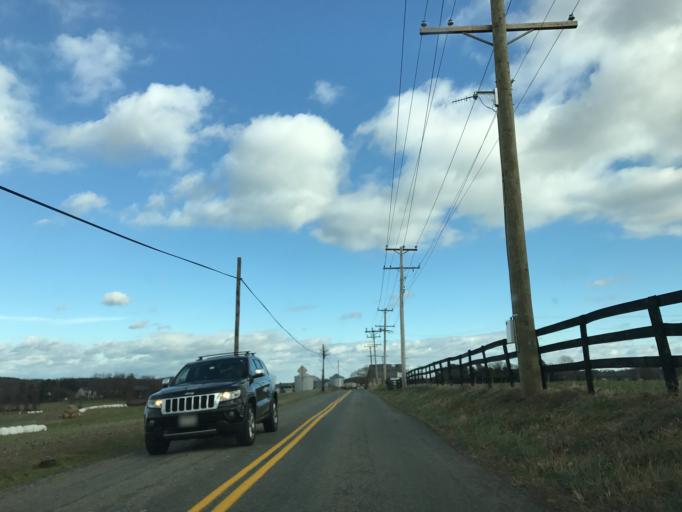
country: US
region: Maryland
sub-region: Harford County
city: Jarrettsville
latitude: 39.6351
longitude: -76.5619
